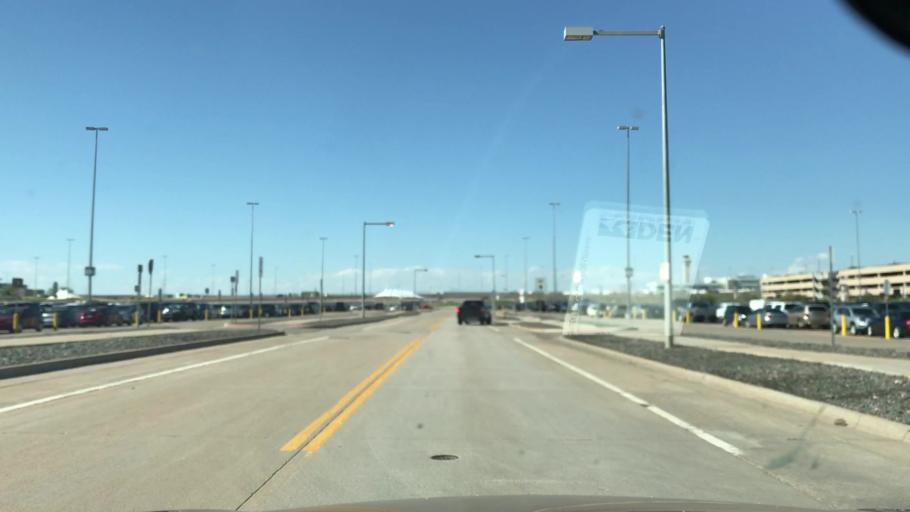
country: US
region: Colorado
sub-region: Weld County
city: Lochbuie
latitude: 39.8465
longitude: -104.6793
